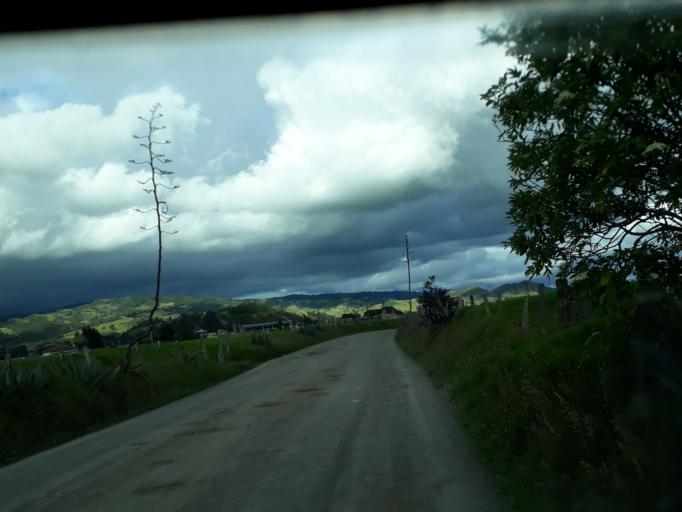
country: CO
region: Cundinamarca
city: Carmen de Carupa
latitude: 5.3510
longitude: -73.9088
